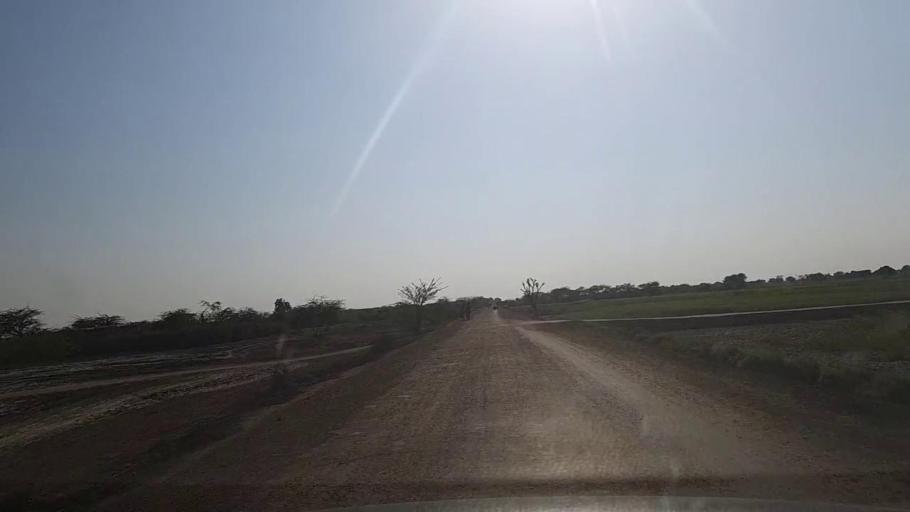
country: PK
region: Sindh
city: Digri
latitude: 25.0375
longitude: 69.2226
